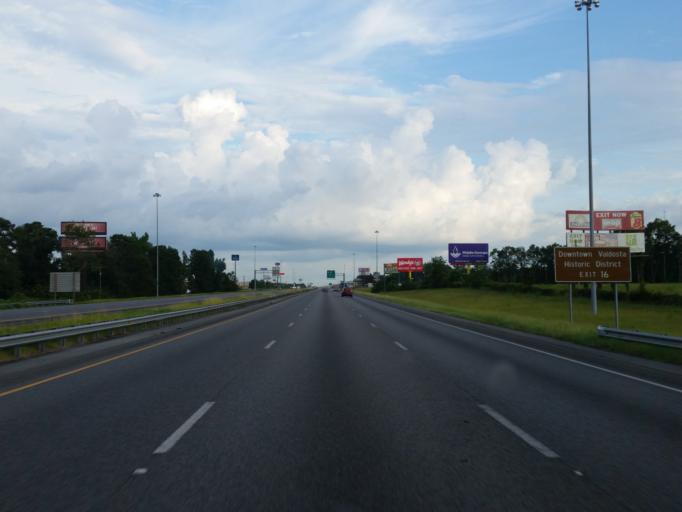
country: US
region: Georgia
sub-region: Lowndes County
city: Remerton
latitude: 30.8317
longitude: -83.3245
